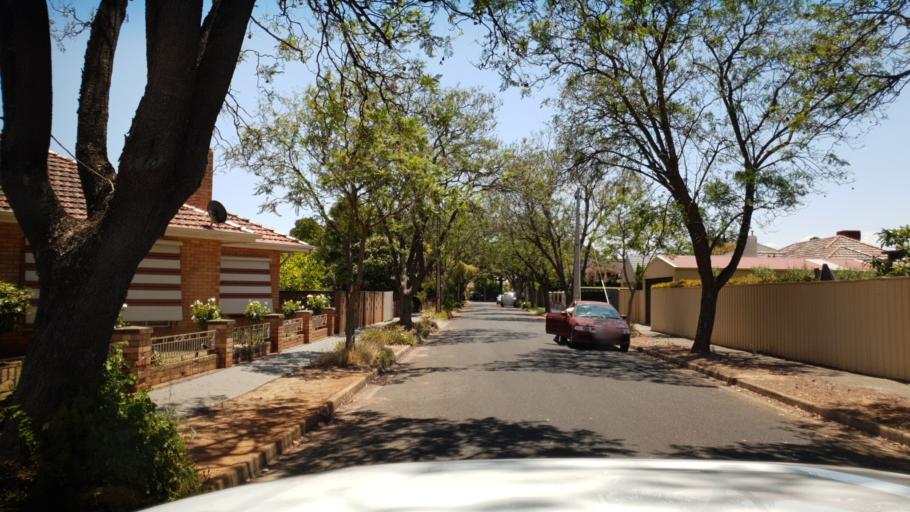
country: AU
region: South Australia
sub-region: Mitcham
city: Clarence Gardens
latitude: -34.9772
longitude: 138.5905
